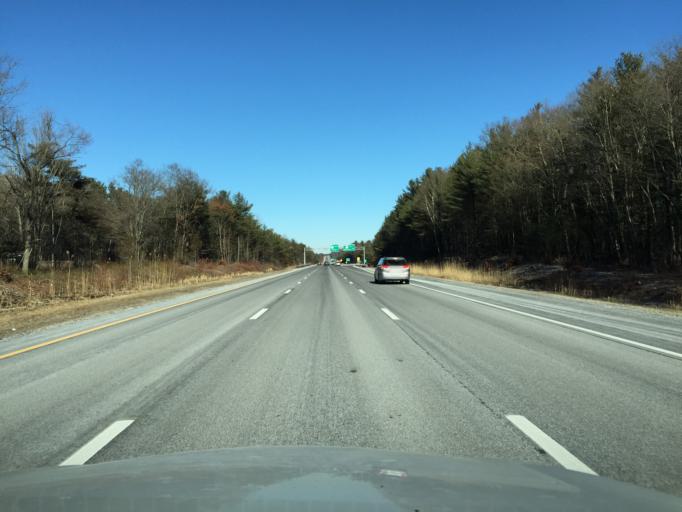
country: US
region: Massachusetts
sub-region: Bristol County
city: Mansfield
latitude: 42.0371
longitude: -71.2464
